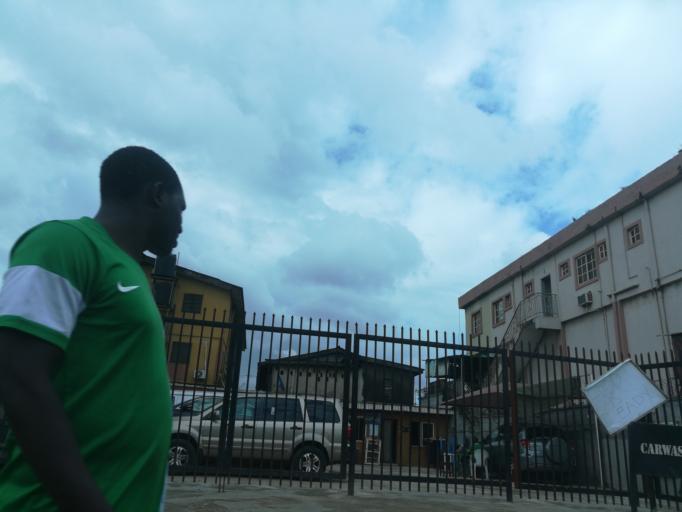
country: NG
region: Lagos
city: Agege
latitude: 6.6182
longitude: 3.3322
